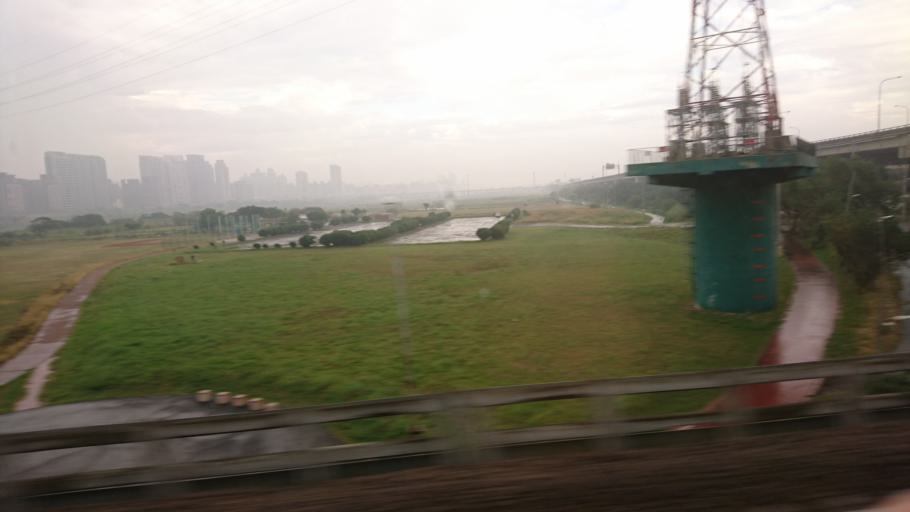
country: TW
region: Taiwan
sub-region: Hsinchu
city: Zhubei
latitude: 24.8194
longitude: 120.9979
